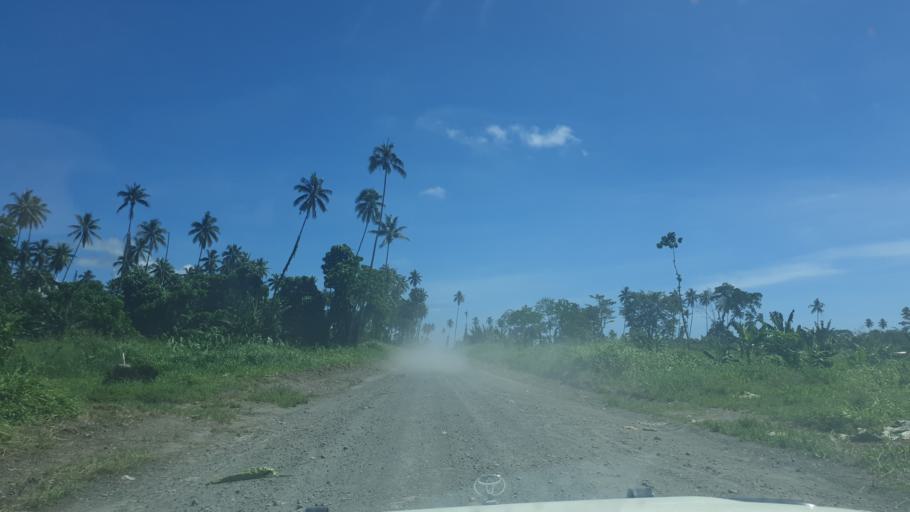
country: PG
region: Bougainville
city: Arawa
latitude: -5.9776
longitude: 155.3506
